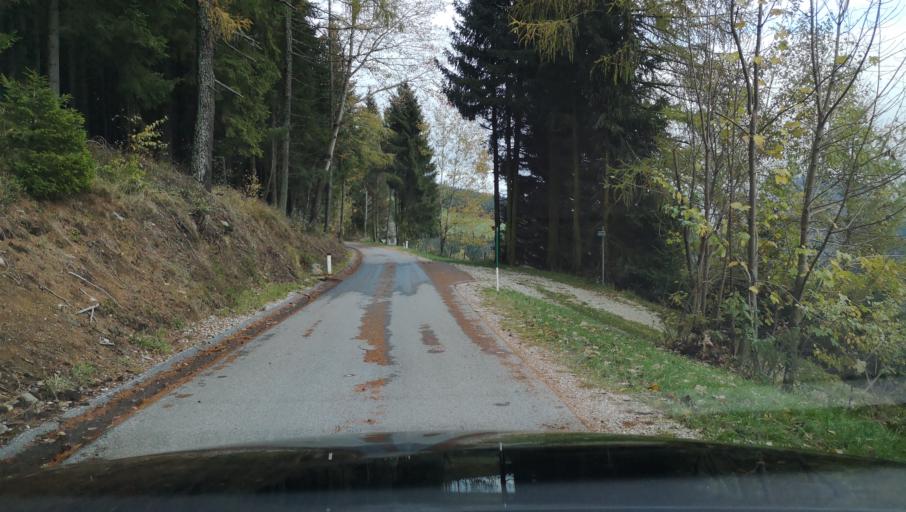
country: AT
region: Styria
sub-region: Politischer Bezirk Weiz
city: Gasen
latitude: 47.3597
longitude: 15.5984
